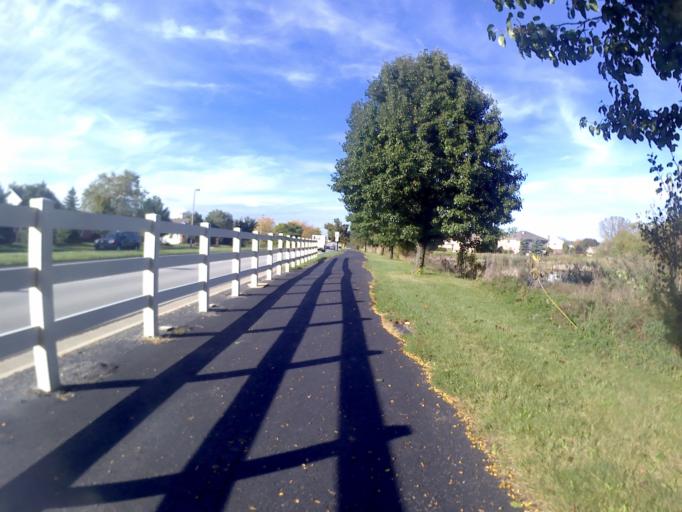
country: US
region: Illinois
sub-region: DuPage County
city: Woodridge
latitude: 41.7206
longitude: -88.0270
